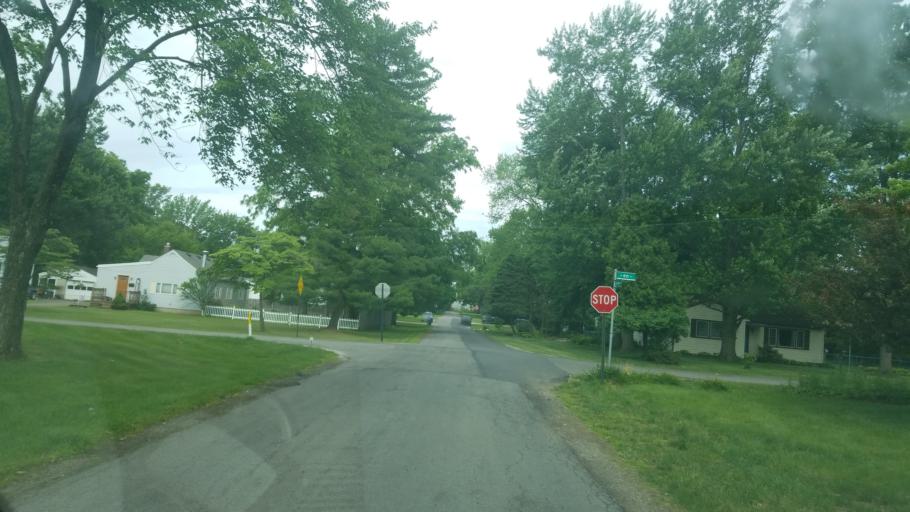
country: US
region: Ohio
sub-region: Franklin County
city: Worthington
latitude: 40.0553
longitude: -82.9943
